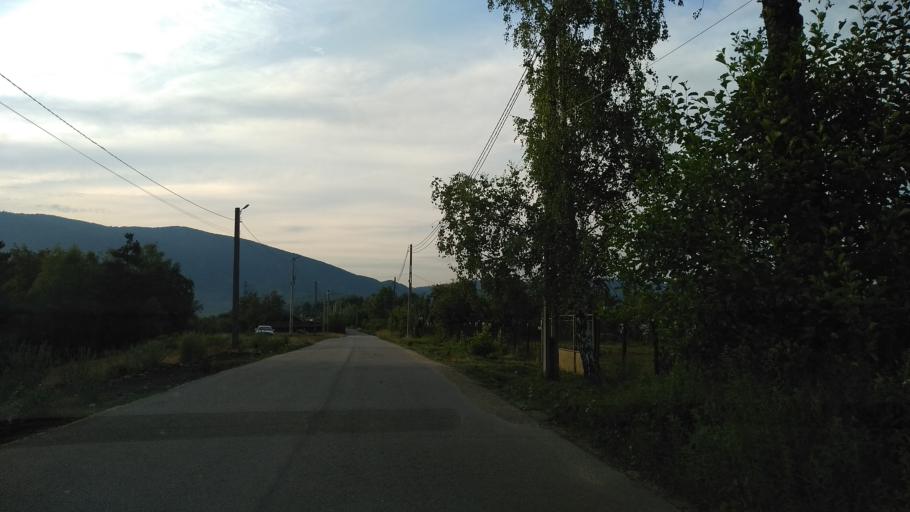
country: RO
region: Hunedoara
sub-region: Municipiul  Vulcan
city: Jiu-Paroseni
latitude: 45.3572
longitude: 23.2887
